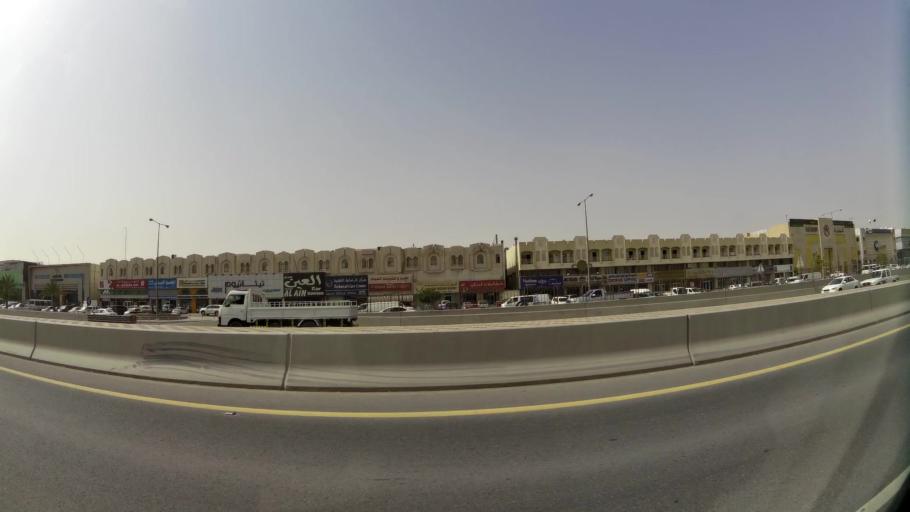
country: QA
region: Baladiyat ar Rayyan
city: Ar Rayyan
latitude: 25.2420
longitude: 51.4601
